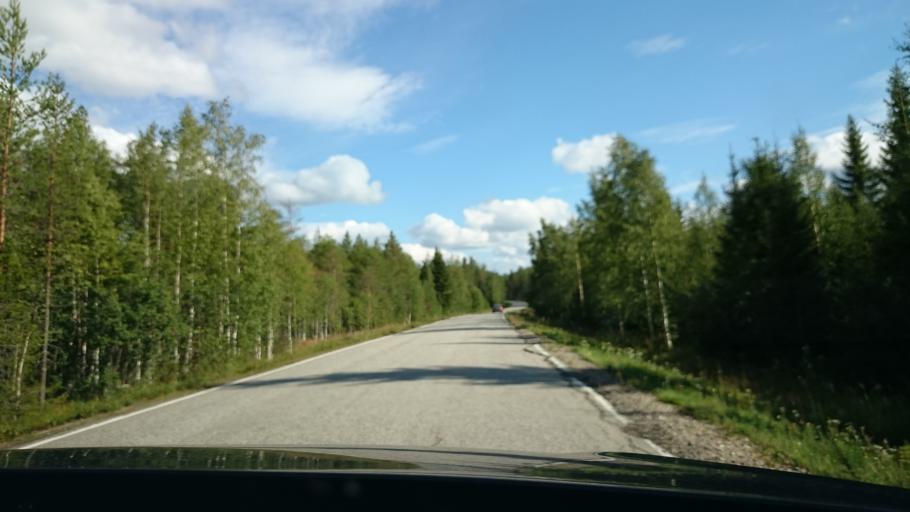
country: FI
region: Kainuu
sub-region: Kehys-Kainuu
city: Suomussalmi
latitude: 64.7548
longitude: 29.4144
